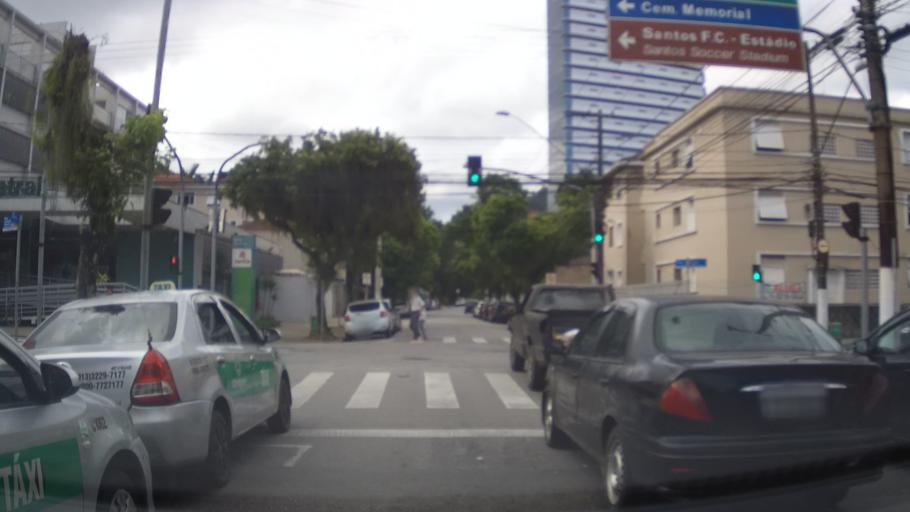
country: BR
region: Sao Paulo
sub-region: Santos
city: Santos
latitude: -23.9491
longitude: -46.3343
